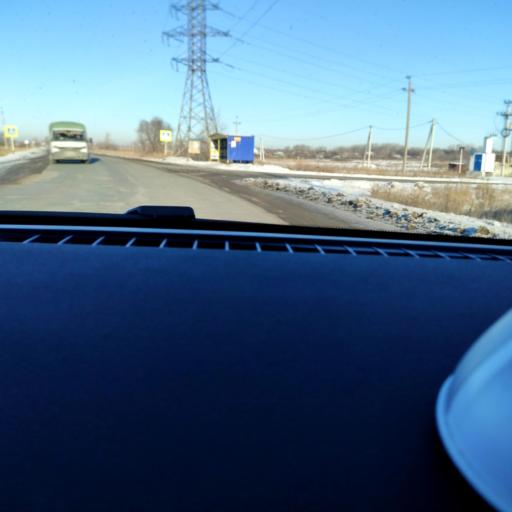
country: RU
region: Samara
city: Spiridonovka
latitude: 53.1115
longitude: 50.6388
